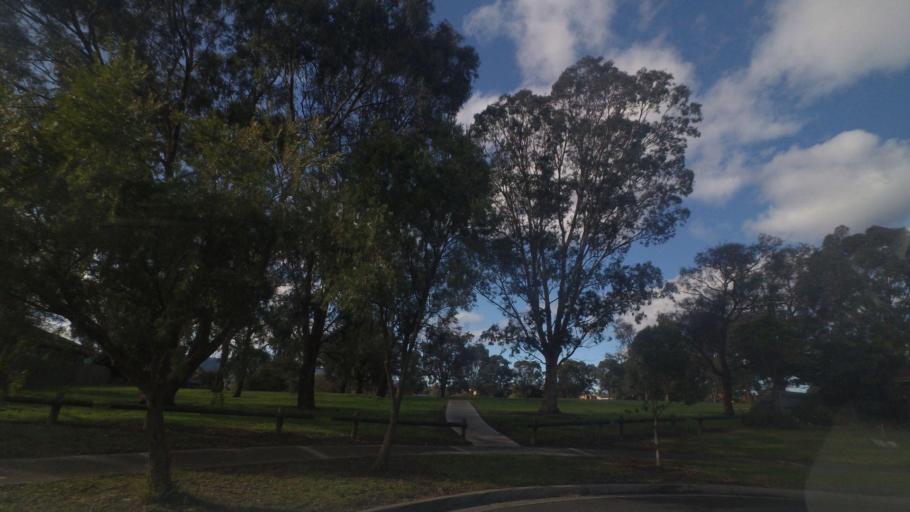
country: AU
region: Victoria
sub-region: Yarra Ranges
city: Lysterfield
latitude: -37.9183
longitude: 145.2730
